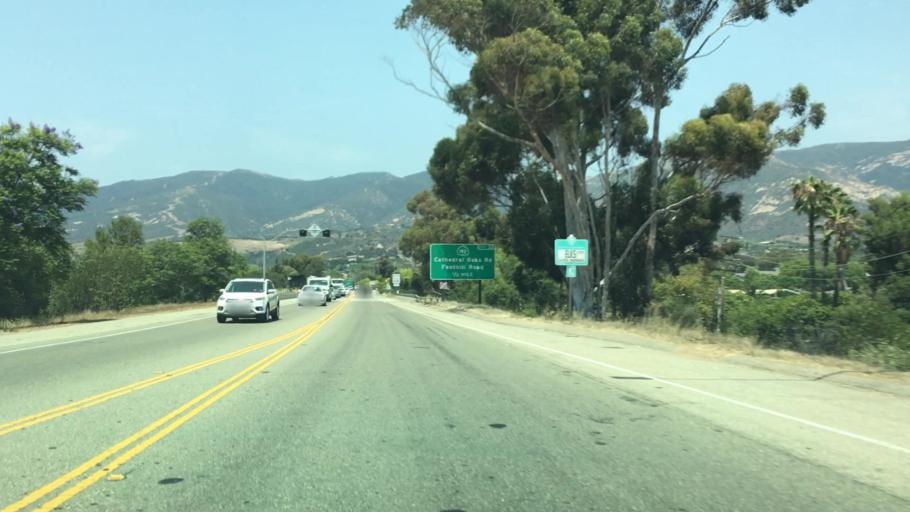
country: US
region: California
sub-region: Santa Barbara County
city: Mission Canyon
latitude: 34.4433
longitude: -119.7599
